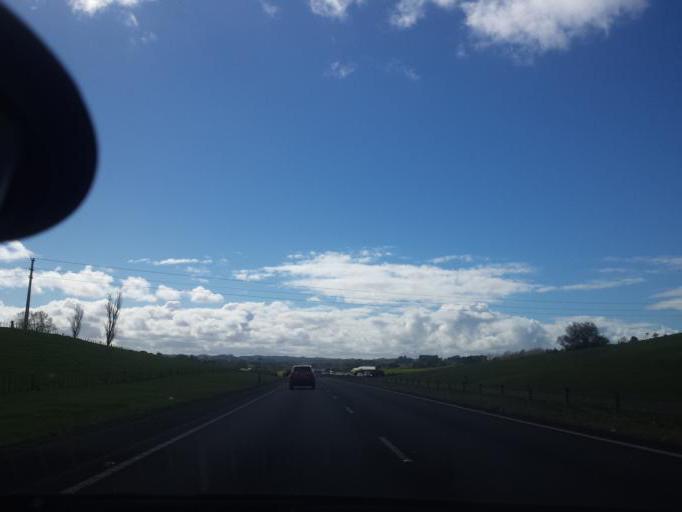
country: NZ
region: Auckland
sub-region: Auckland
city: Rothesay Bay
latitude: -36.6425
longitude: 174.6626
